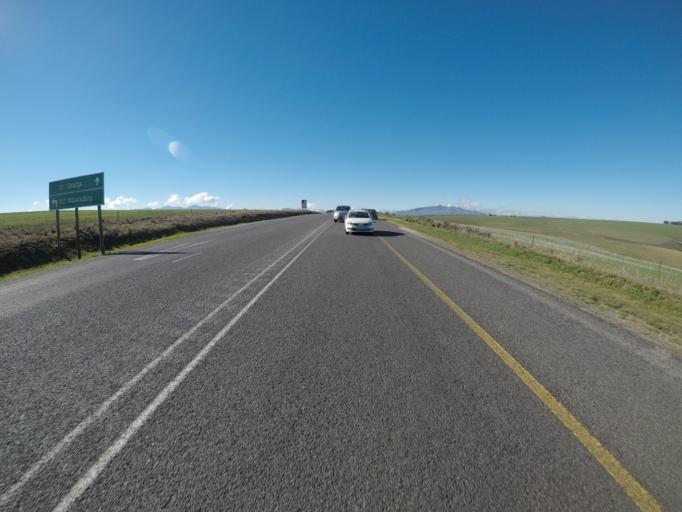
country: ZA
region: Western Cape
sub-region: Overberg District Municipality
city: Caledon
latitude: -34.2247
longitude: 19.2763
